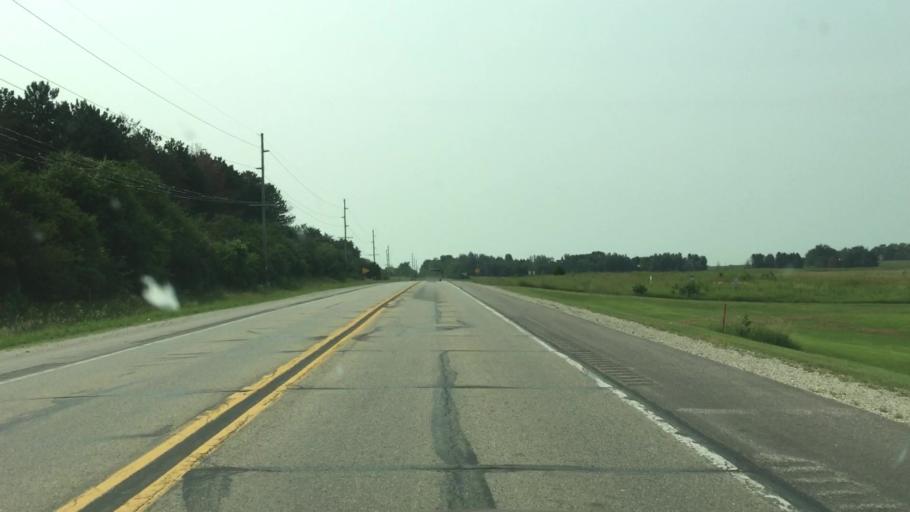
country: US
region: Iowa
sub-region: Dickinson County
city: Milford
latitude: 43.3503
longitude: -95.1798
